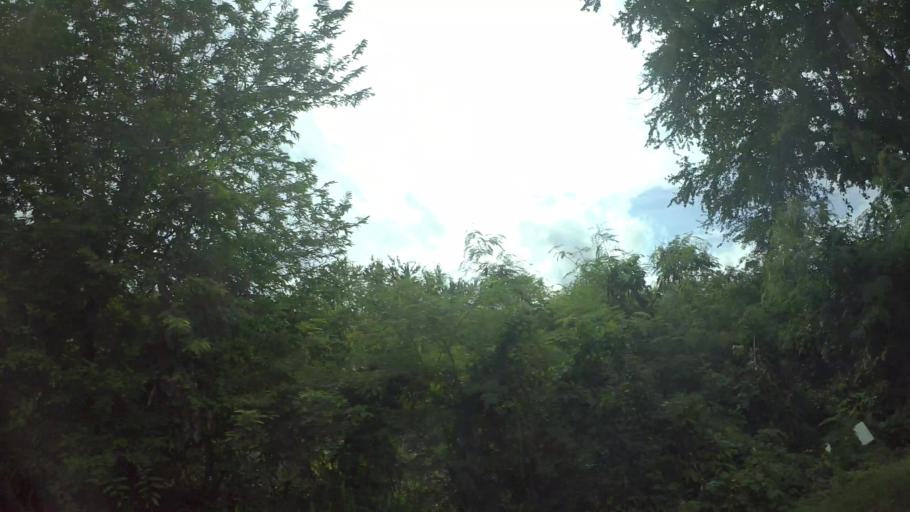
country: TH
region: Rayong
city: Rayong
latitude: 12.6659
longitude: 101.2805
